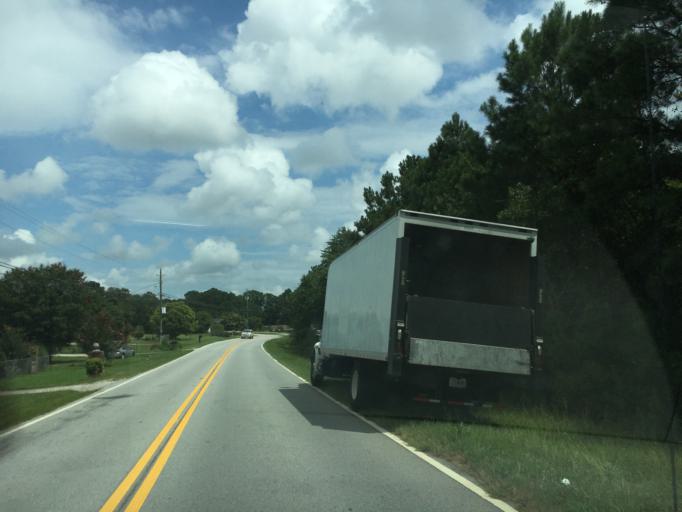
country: US
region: Georgia
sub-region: Rockdale County
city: Lakeview Estates
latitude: 33.6933
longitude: -84.0376
